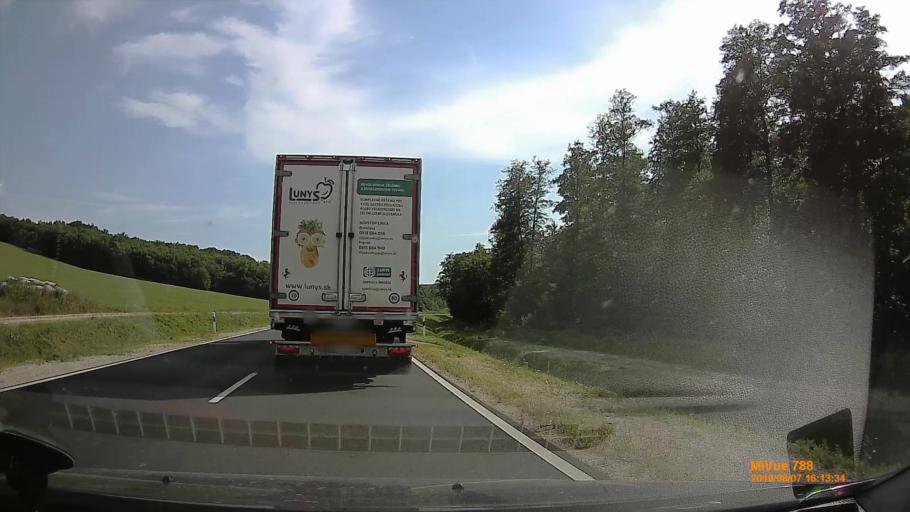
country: HU
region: Zala
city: Zalalovo
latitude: 46.8417
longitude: 16.6285
